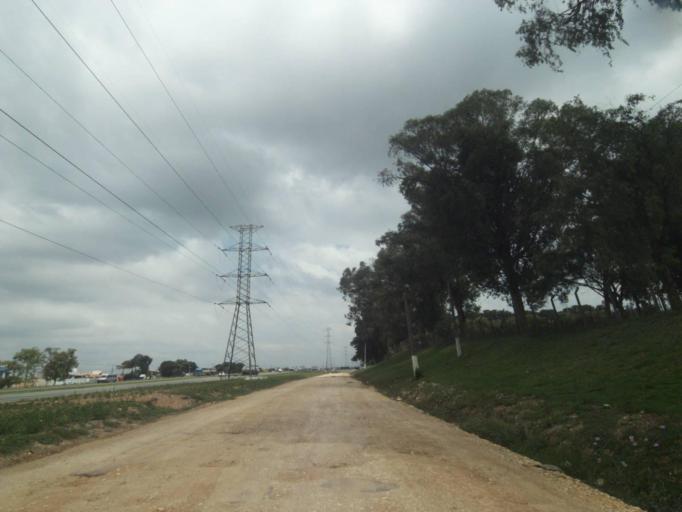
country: BR
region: Parana
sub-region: Curitiba
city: Curitiba
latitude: -25.4741
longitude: -49.3527
